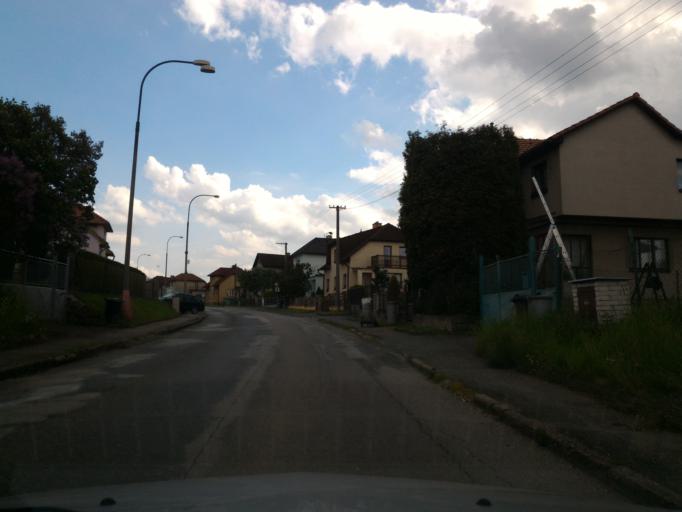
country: CZ
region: Vysocina
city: Ledec nad Sazavou
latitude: 49.6900
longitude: 15.2823
